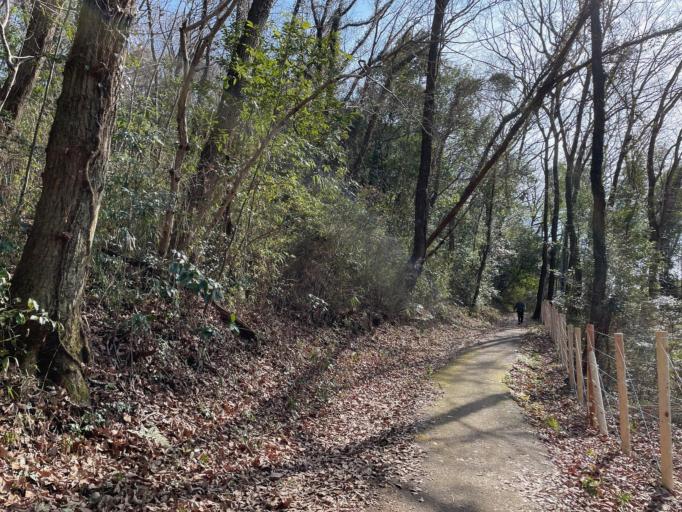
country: JP
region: Tokyo
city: Higashimurayama-shi
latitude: 35.7606
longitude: 139.3969
